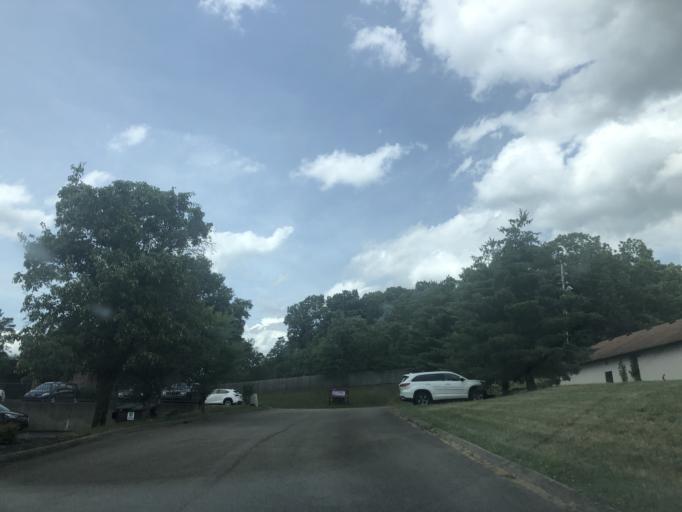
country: US
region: Tennessee
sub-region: Davidson County
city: Belle Meade
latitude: 36.0767
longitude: -86.9234
